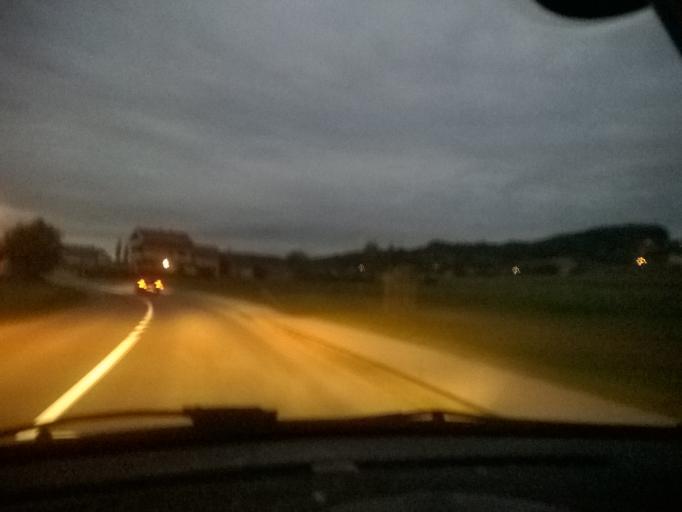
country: HR
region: Krapinsko-Zagorska
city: Zabok
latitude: 46.0596
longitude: 15.9259
